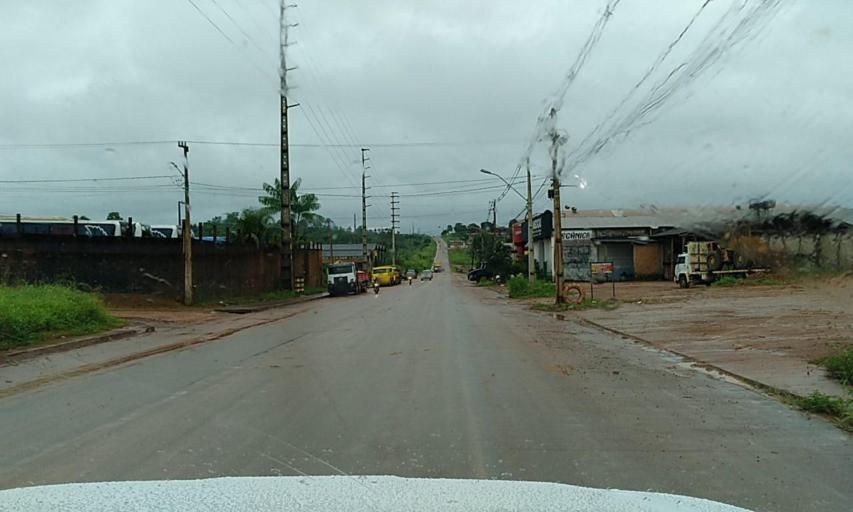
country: BR
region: Para
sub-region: Altamira
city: Altamira
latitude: -3.2156
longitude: -52.2400
